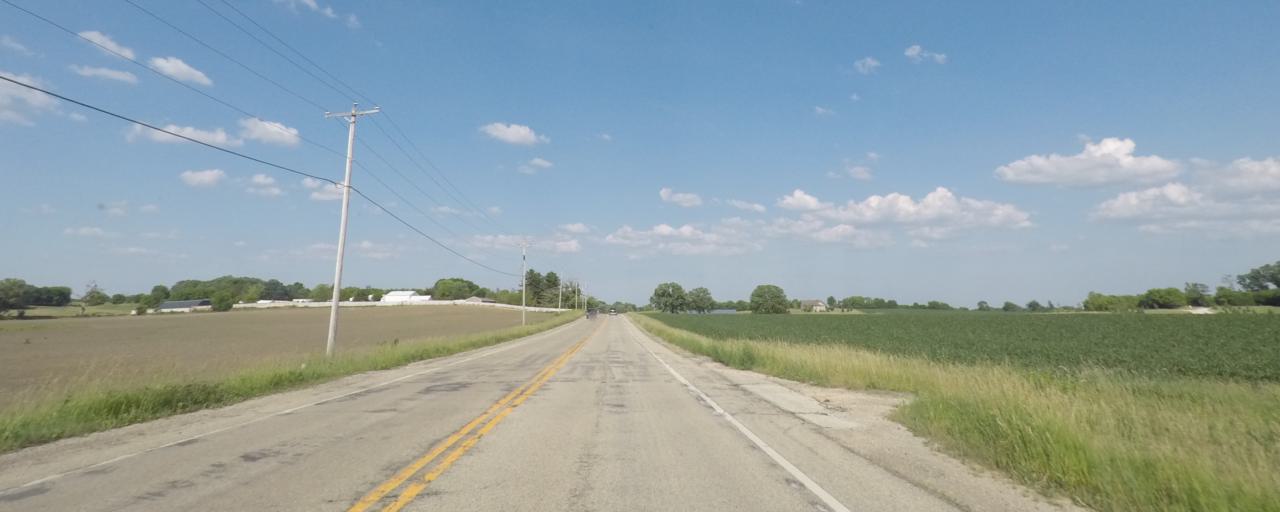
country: US
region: Wisconsin
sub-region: Waukesha County
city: Mukwonago
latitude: 42.8329
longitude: -88.2905
